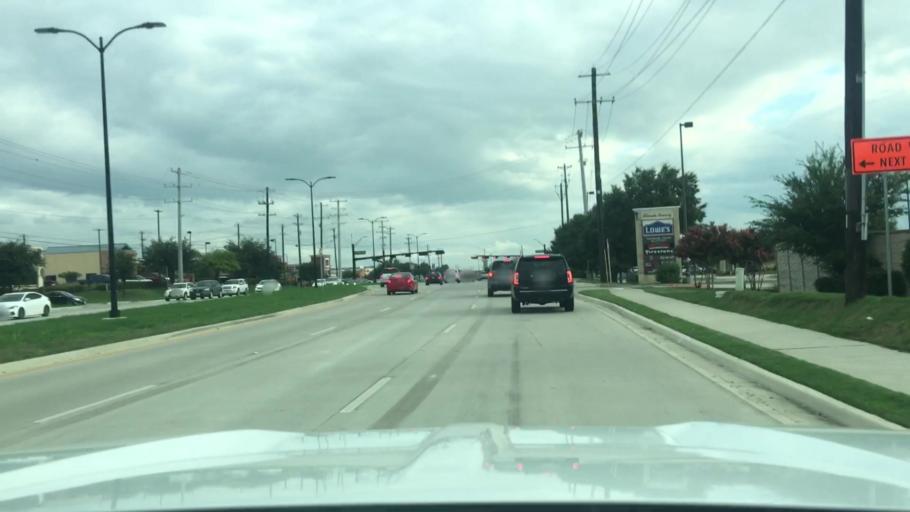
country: US
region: Texas
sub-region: Denton County
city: Little Elm
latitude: 33.1803
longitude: -96.8874
